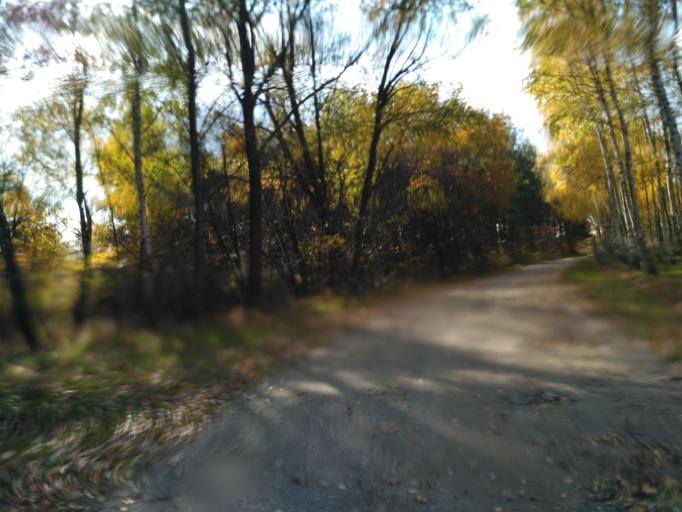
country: PL
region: Subcarpathian Voivodeship
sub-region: Powiat rzeszowski
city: Rudna Wielka
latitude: 50.1256
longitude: 21.9095
